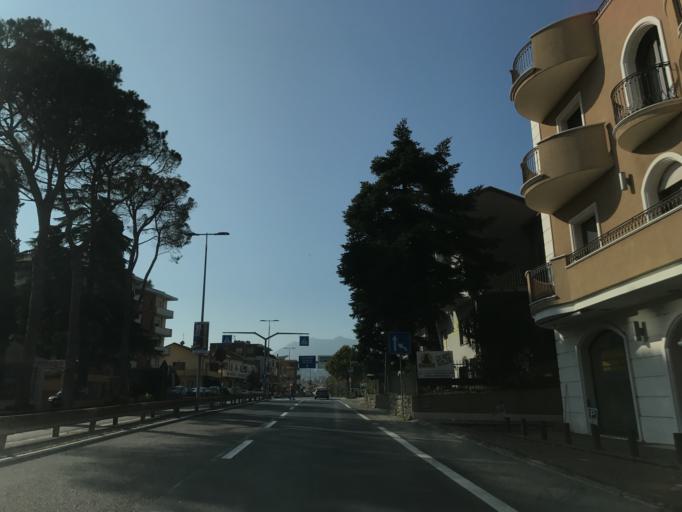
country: SM
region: Serravalle
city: Serravalle
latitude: 43.9817
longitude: 12.4901
